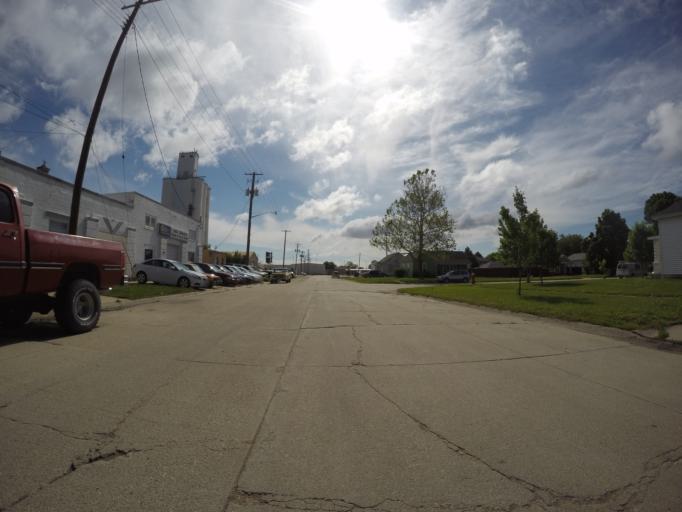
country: US
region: Nebraska
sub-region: Buffalo County
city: Kearney
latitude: 40.6935
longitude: -99.0877
